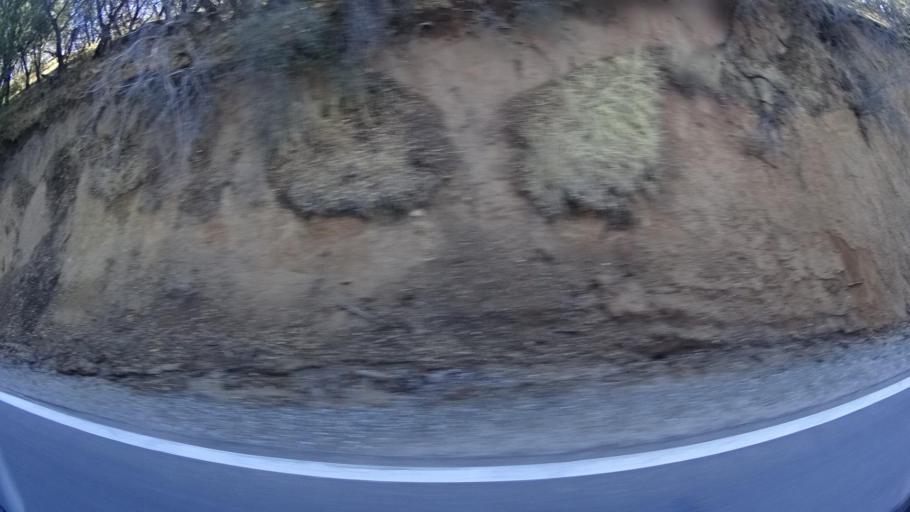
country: US
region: California
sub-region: Kern County
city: Alta Sierra
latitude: 35.7372
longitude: -118.6544
